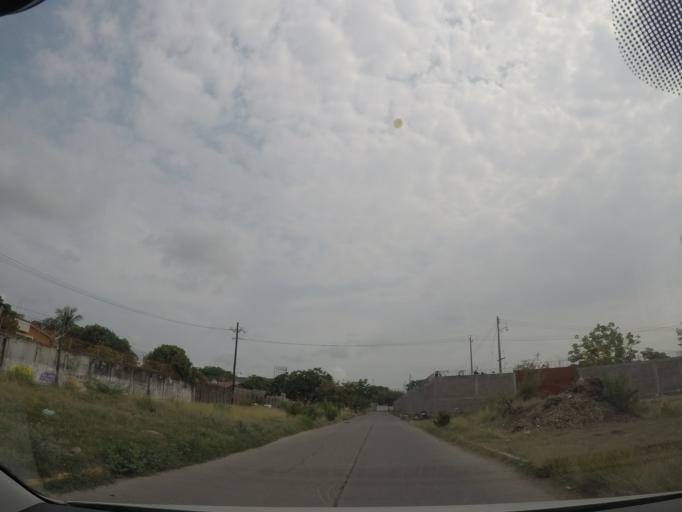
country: MX
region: Oaxaca
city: Juchitan de Zaragoza
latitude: 16.4452
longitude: -95.0214
